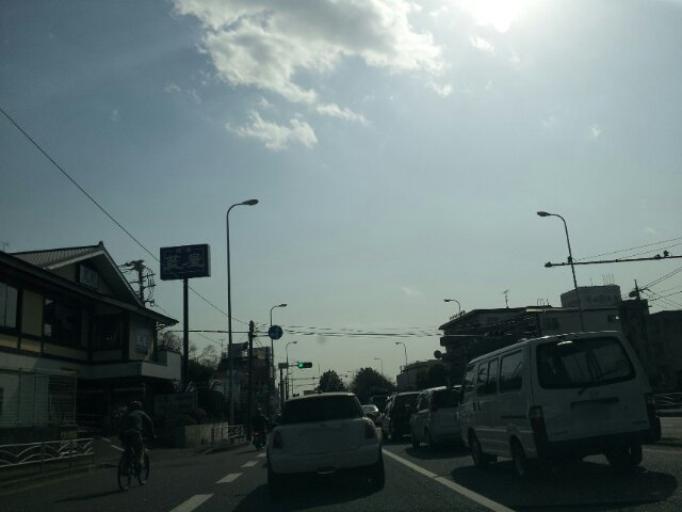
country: JP
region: Kanagawa
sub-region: Kawasaki-shi
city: Kawasaki
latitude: 35.5095
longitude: 139.6622
